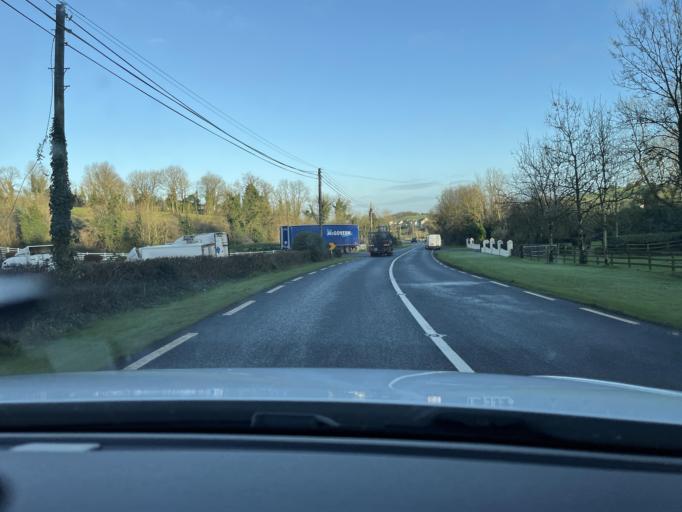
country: IE
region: Ulster
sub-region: An Cabhan
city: Ballyconnell
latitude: 54.1165
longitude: -7.6118
